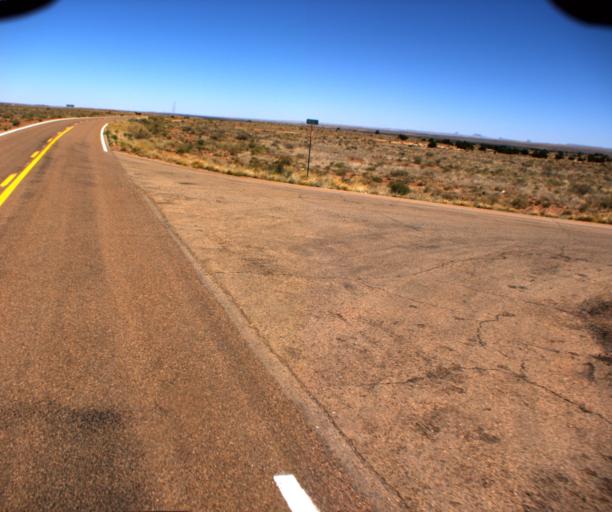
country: US
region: Arizona
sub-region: Navajo County
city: Winslow
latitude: 34.9415
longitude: -110.6439
